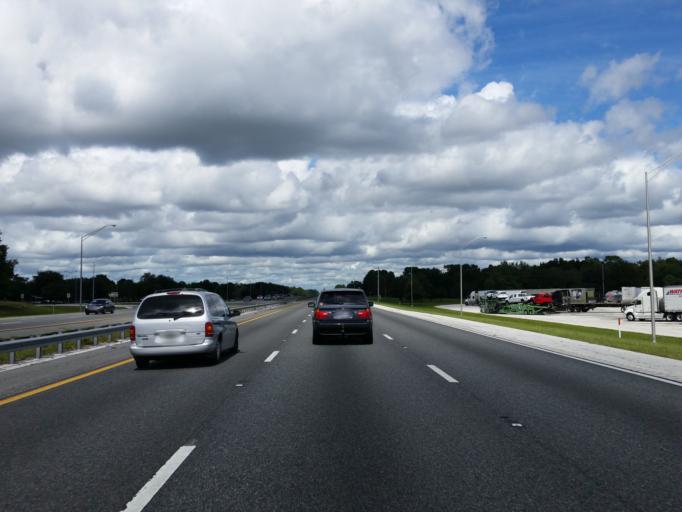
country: US
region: Florida
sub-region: Marion County
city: Ocala
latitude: 29.0917
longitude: -82.1849
